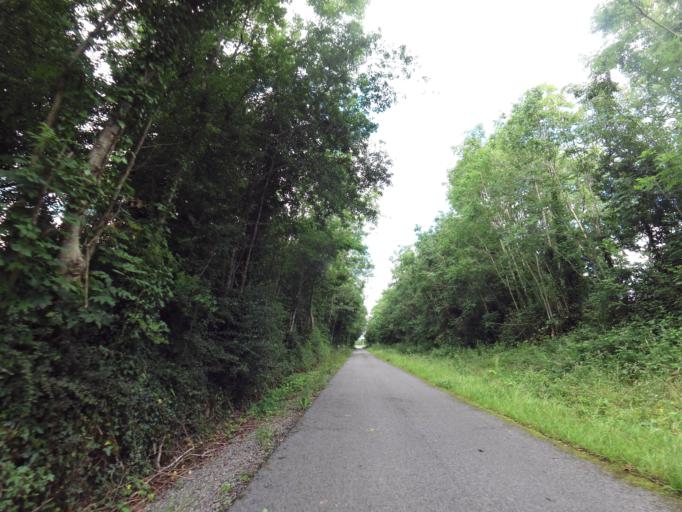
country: IE
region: Leinster
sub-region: An Iarmhi
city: Kilbeggan
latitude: 53.4551
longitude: -7.5217
